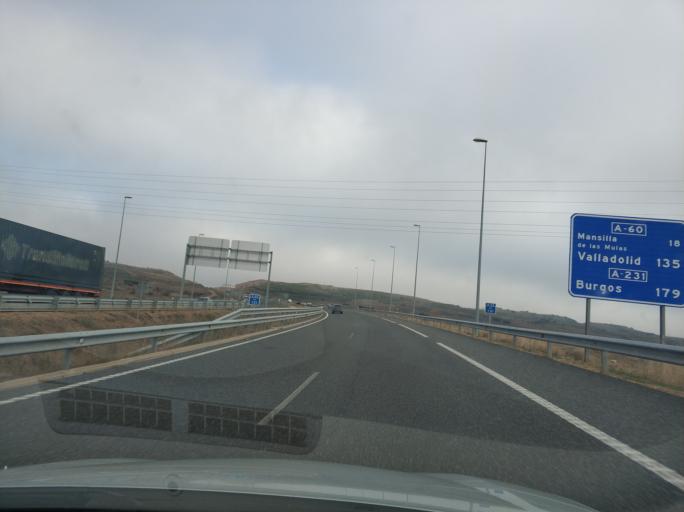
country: ES
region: Castille and Leon
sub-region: Provincia de Leon
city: Leon
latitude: 42.5650
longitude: -5.5417
